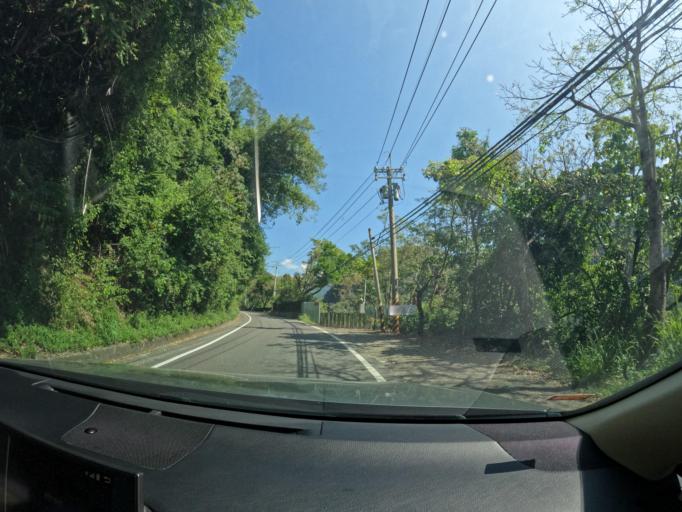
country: TW
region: Taiwan
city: Yujing
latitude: 23.1135
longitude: 120.7131
